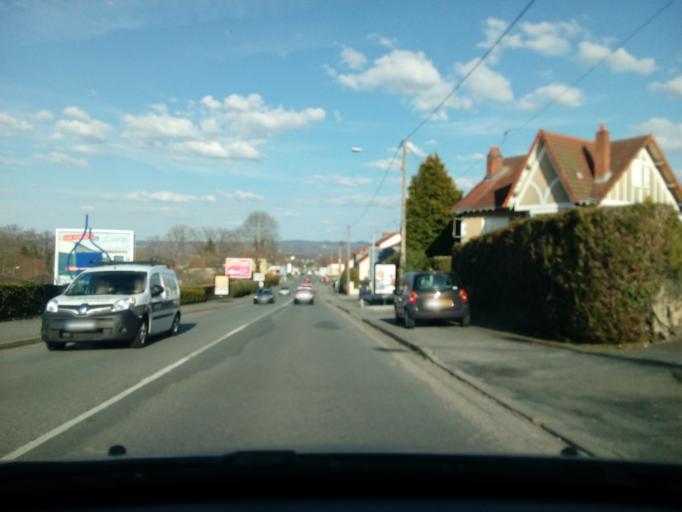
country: FR
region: Limousin
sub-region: Departement de la Creuse
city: Gueret
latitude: 46.1744
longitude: 1.8874
